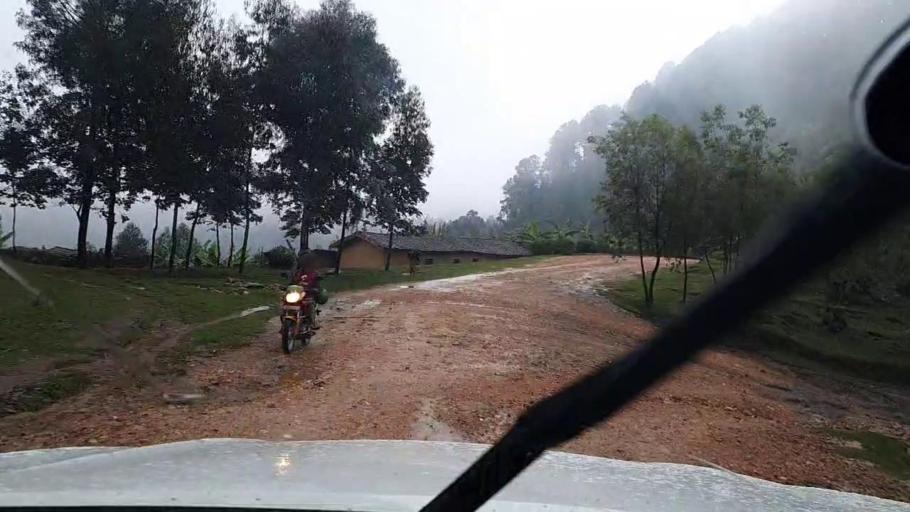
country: RW
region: Western Province
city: Kibuye
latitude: -2.1361
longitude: 29.4646
